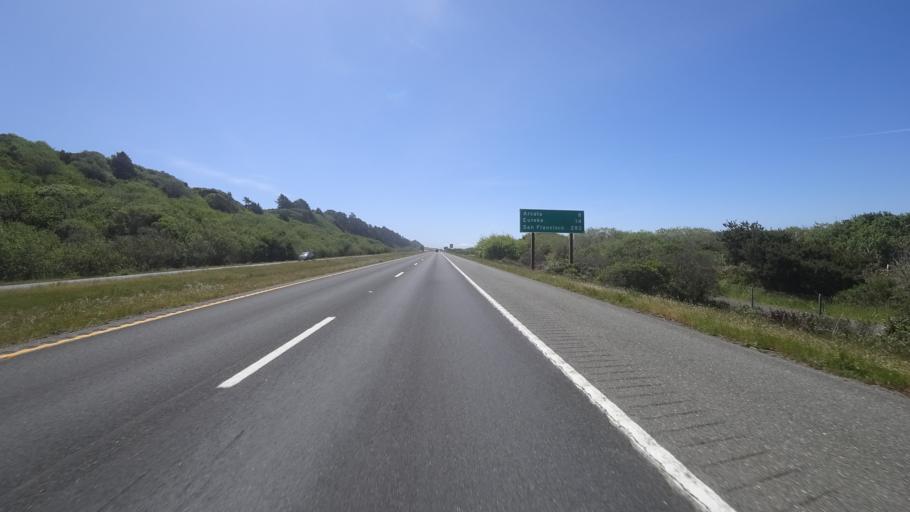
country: US
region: California
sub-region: Humboldt County
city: McKinleyville
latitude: 40.9879
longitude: -124.1159
